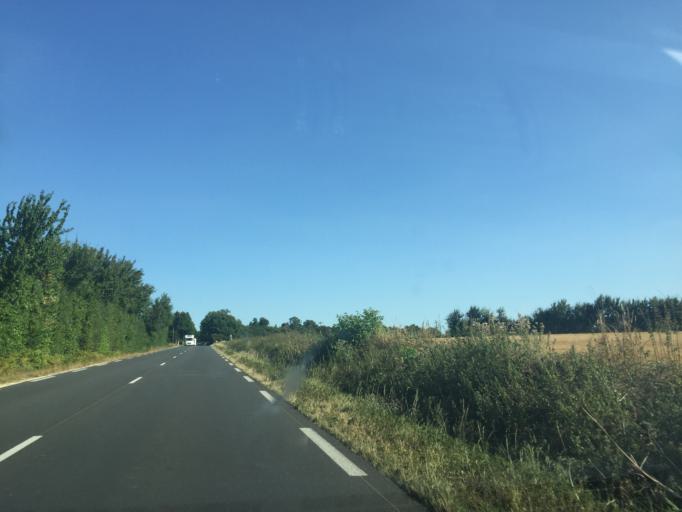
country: FR
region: Poitou-Charentes
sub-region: Departement des Deux-Sevres
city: Melle
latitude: 46.2117
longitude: -0.1125
